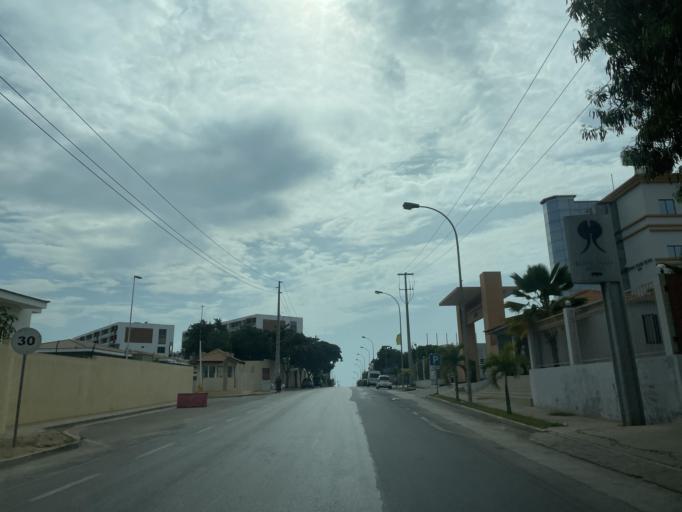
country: AO
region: Luanda
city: Luanda
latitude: -8.9215
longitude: 13.1745
